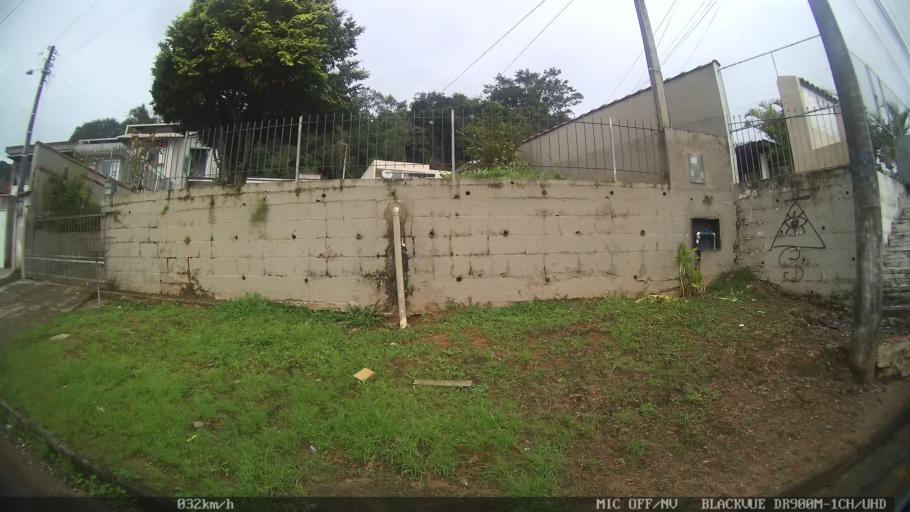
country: BR
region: Santa Catarina
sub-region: Biguacu
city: Biguacu
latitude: -27.5180
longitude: -48.6463
